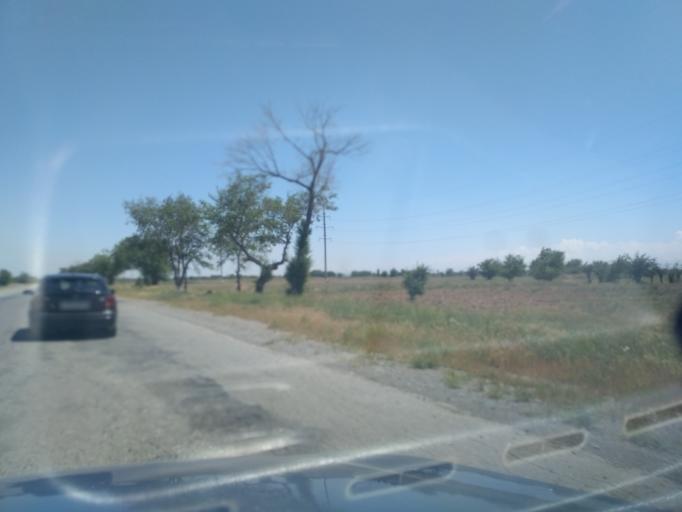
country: TJ
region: Viloyati Sughd
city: Zafarobod
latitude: 40.2183
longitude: 68.8997
